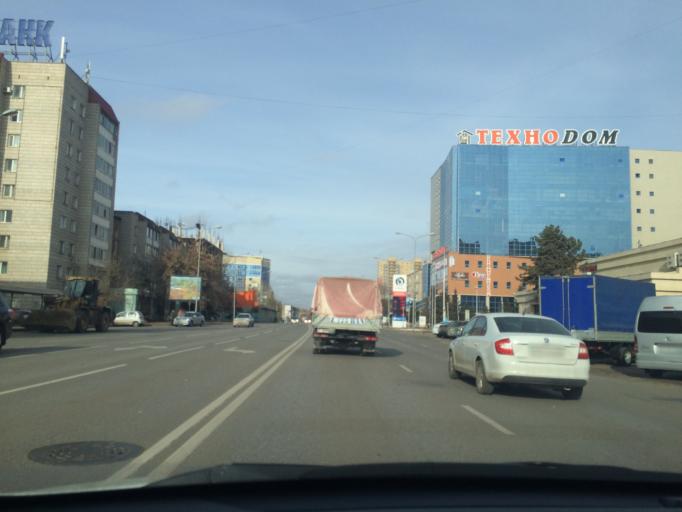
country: KZ
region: Astana Qalasy
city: Astana
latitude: 51.1717
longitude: 71.4257
